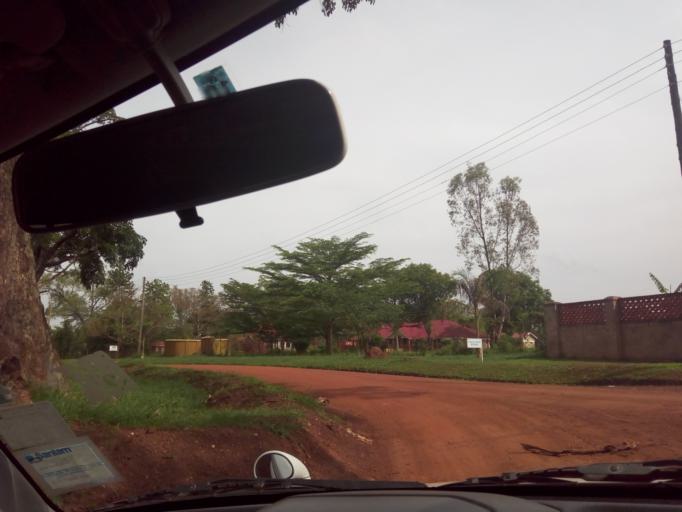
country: UG
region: Western Region
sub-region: Masindi District
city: Masindi
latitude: 1.6912
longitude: 31.7221
